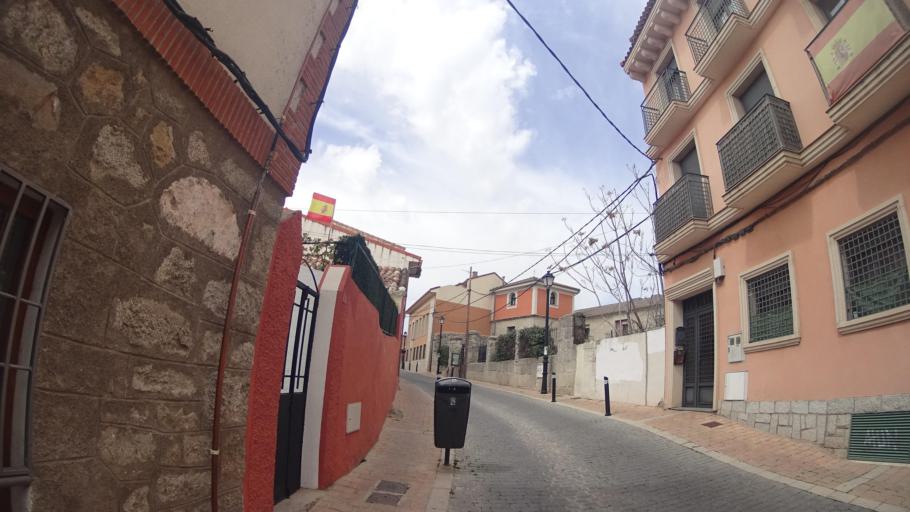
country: ES
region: Madrid
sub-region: Provincia de Madrid
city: Colmenar Viejo
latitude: 40.6577
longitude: -3.7674
